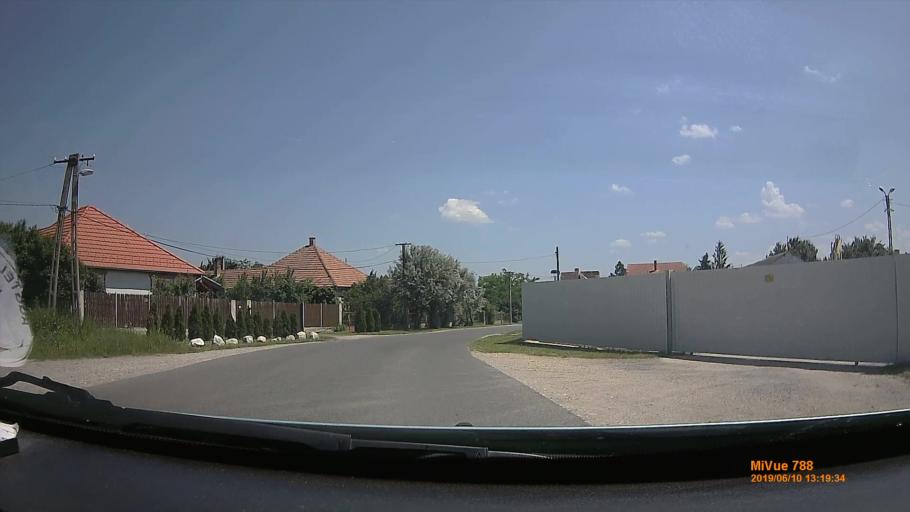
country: HU
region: Borsod-Abauj-Zemplen
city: Tiszaluc
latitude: 48.0408
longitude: 21.0755
